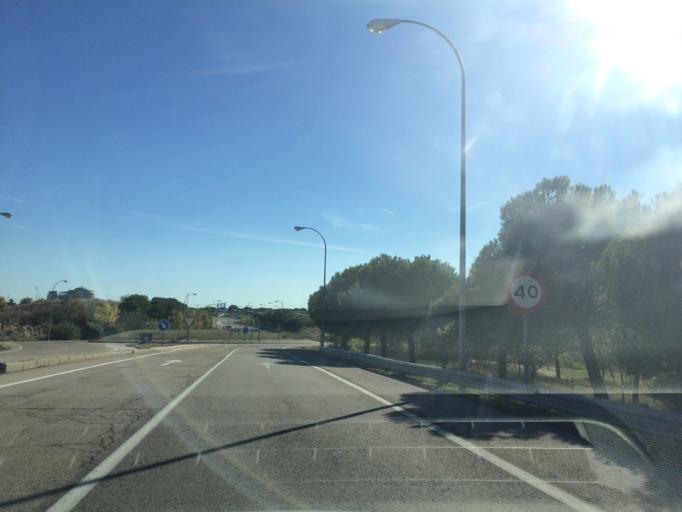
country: ES
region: Madrid
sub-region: Provincia de Madrid
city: Tres Cantos
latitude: 40.6066
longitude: -3.7220
